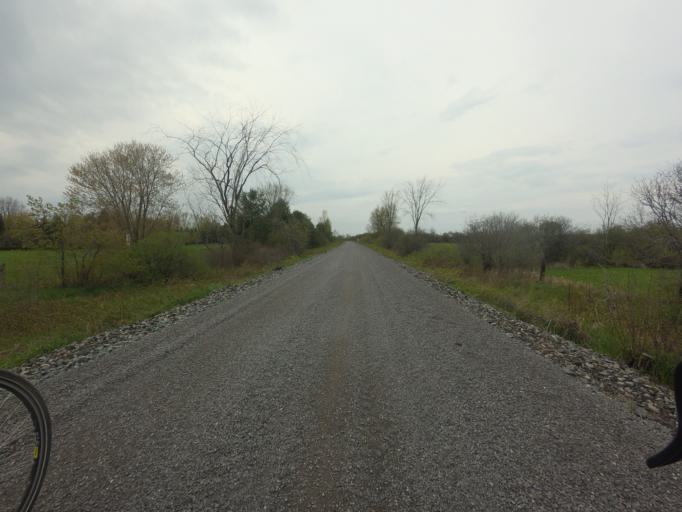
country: CA
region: Ontario
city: Carleton Place
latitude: 45.2037
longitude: -76.1697
